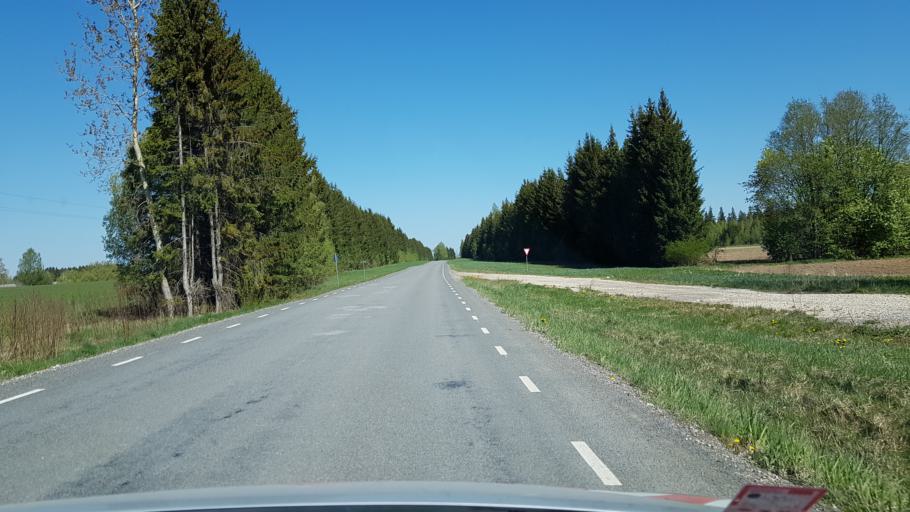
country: EE
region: Vorumaa
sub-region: Voru linn
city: Voru
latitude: 57.9431
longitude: 26.9538
